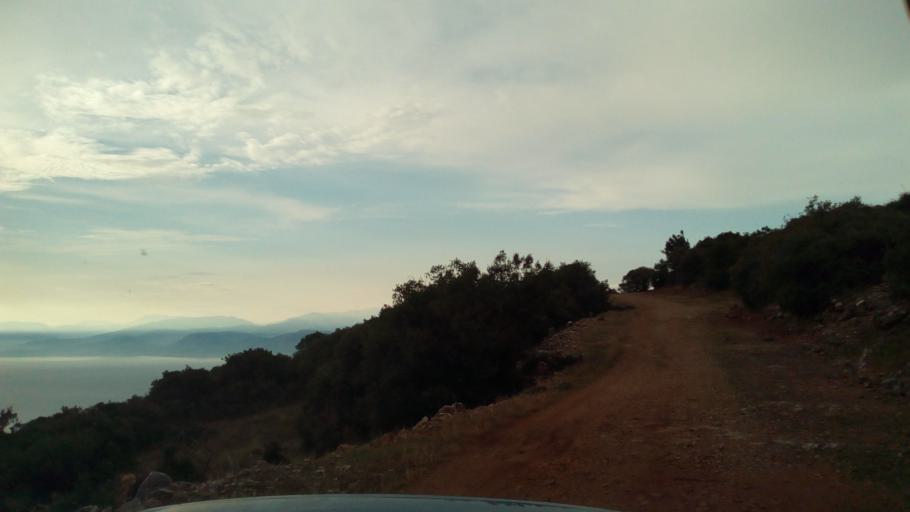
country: GR
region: West Greece
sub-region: Nomos Achaias
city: Kamarai
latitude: 38.4118
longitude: 22.0479
